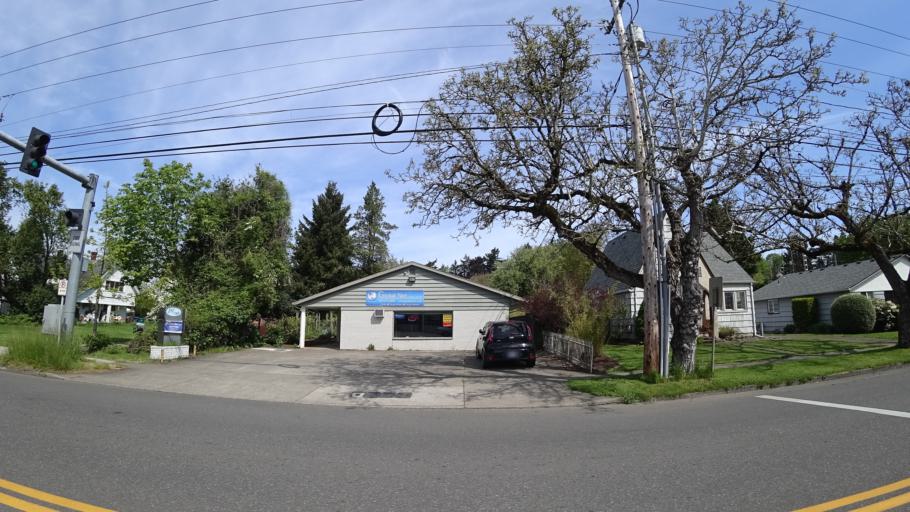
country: US
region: Oregon
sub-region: Clackamas County
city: Milwaukie
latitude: 45.4466
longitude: -122.6283
